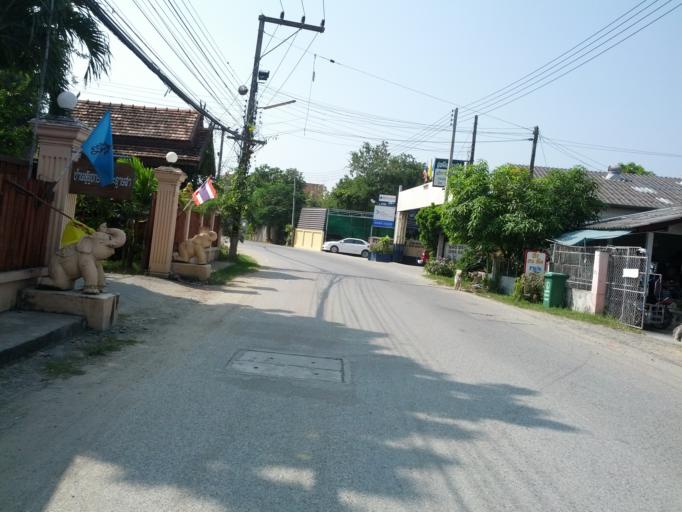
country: TH
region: Chiang Mai
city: San Kamphaeng
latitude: 18.7711
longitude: 99.0753
